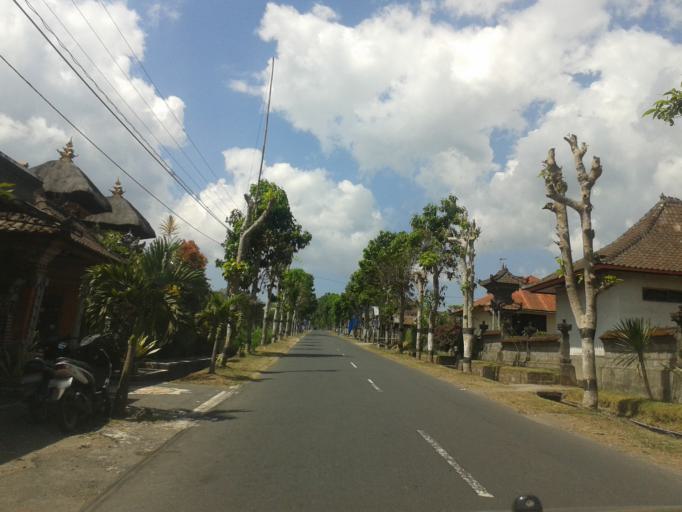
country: ID
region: Bali
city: Banjar Kedisan
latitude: -8.3151
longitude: 115.3319
